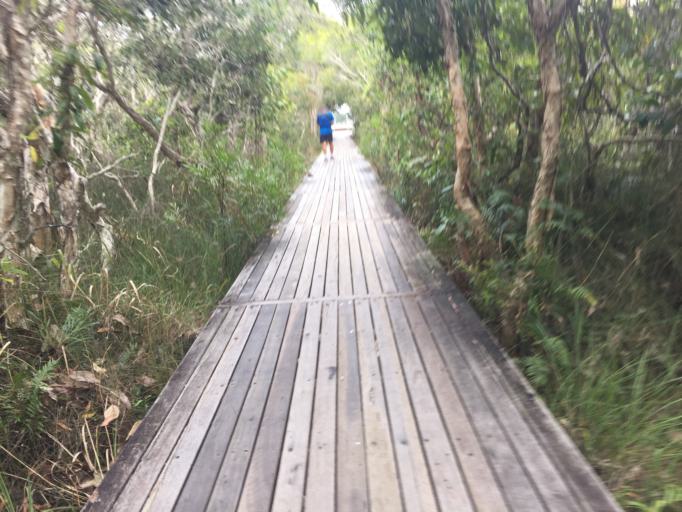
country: AU
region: Queensland
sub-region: Sunshine Coast
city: Coolum Beach
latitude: -26.5748
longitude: 153.0969
